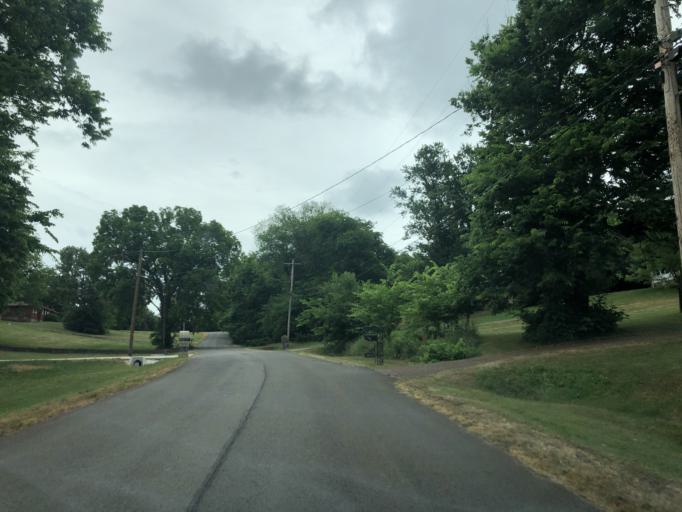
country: US
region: Tennessee
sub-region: Davidson County
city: Goodlettsville
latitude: 36.2644
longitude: -86.7720
